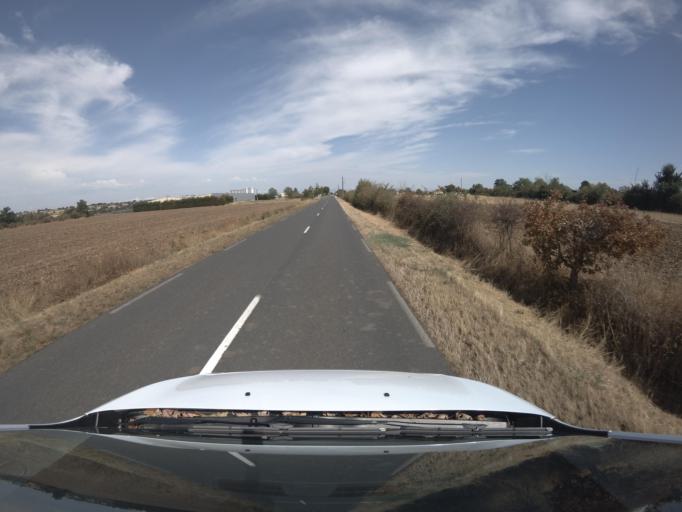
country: FR
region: Poitou-Charentes
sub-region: Departement des Deux-Sevres
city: Argenton-les-Vallees
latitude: 46.9837
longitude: -0.4680
